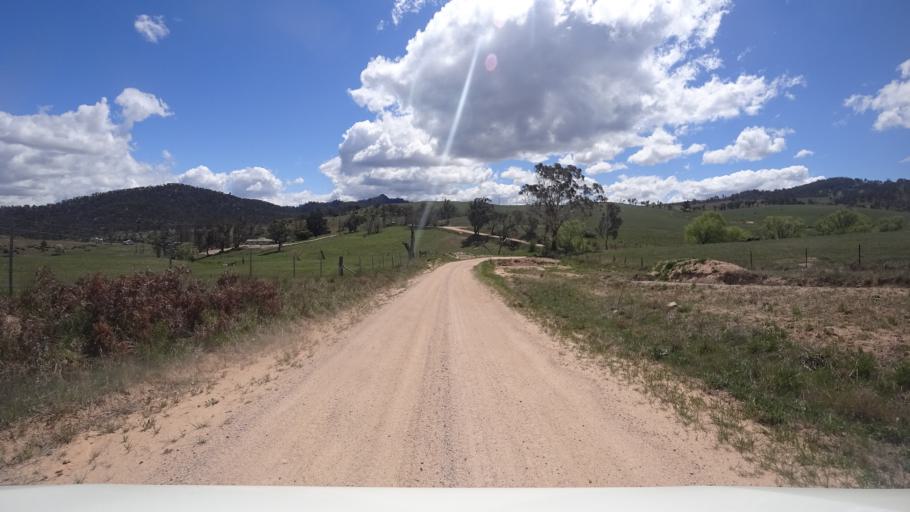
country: AU
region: New South Wales
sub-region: Oberon
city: Oberon
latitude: -33.5668
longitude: 149.9417
